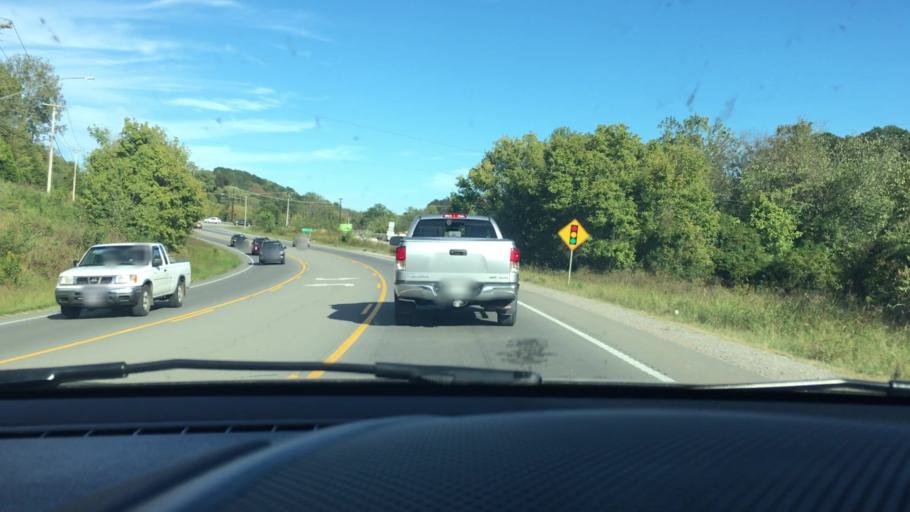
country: US
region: Tennessee
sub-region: Montgomery County
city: Clarksville
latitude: 36.5001
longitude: -87.2930
